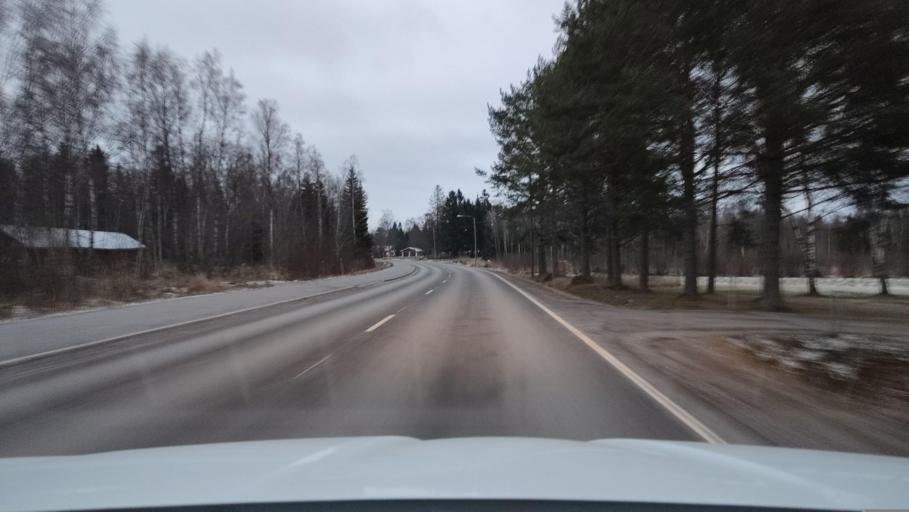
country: FI
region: Ostrobothnia
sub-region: Vaasa
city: Replot
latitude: 63.2216
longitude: 21.4141
